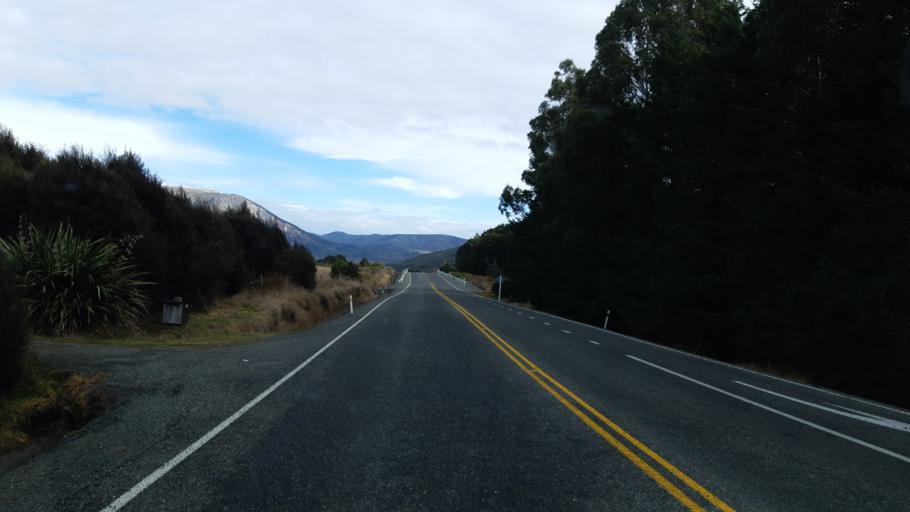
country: NZ
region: Tasman
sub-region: Tasman District
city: Wakefield
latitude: -41.7856
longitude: 172.8931
